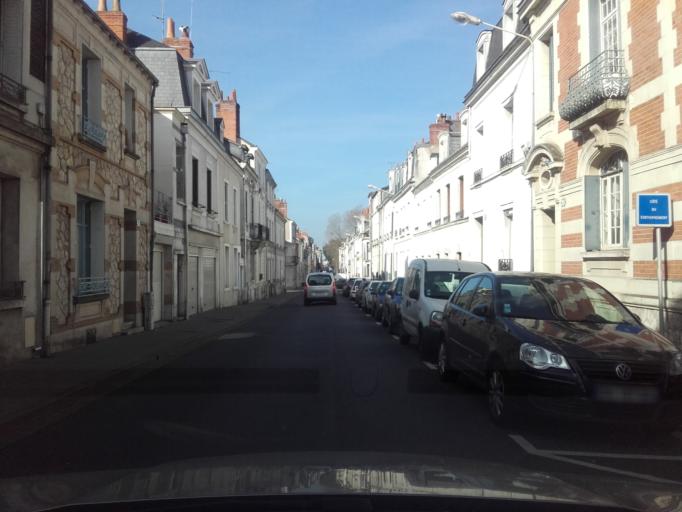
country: FR
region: Centre
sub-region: Departement d'Indre-et-Loire
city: Tours
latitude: 47.3840
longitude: 0.6902
